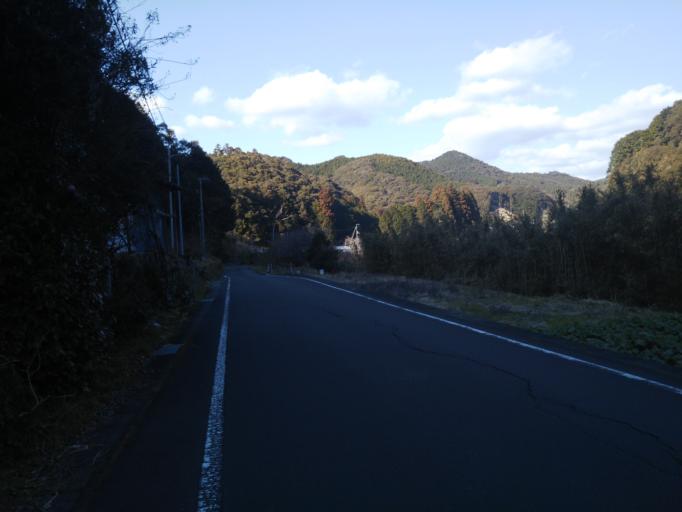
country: JP
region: Kochi
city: Nakamura
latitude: 33.0450
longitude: 132.9704
